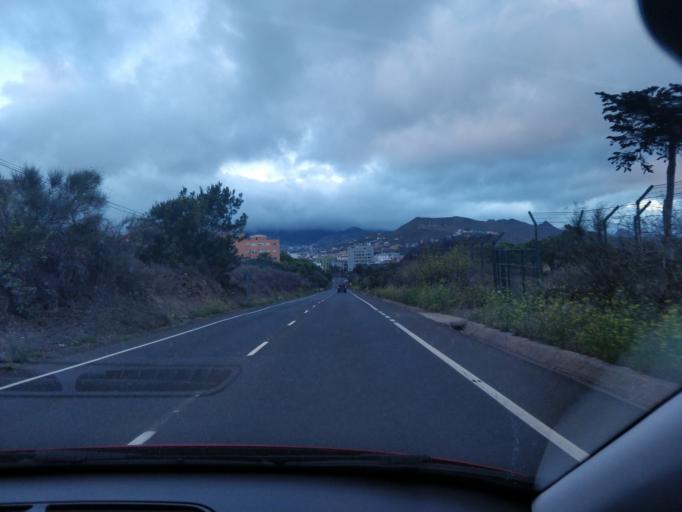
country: ES
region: Canary Islands
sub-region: Provincia de Santa Cruz de Tenerife
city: La Laguna
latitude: 28.4771
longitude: -16.3211
